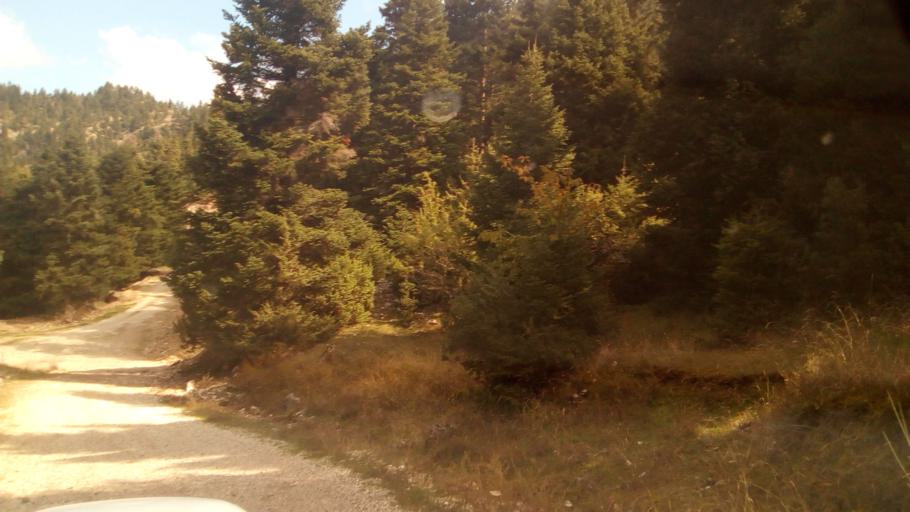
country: GR
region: West Greece
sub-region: Nomos Aitolias kai Akarnanias
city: Thermo
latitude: 38.6506
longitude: 21.9210
